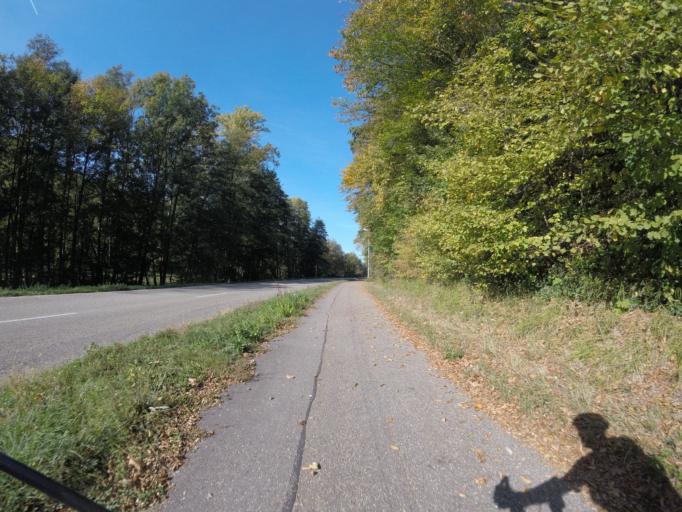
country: DE
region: Baden-Wuerttemberg
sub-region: Karlsruhe Region
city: Bretten
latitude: 49.0128
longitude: 8.7220
